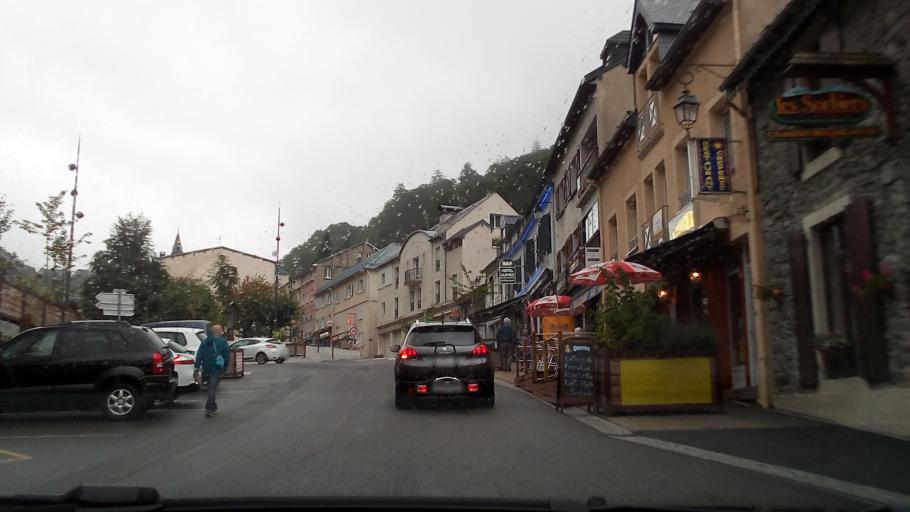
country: FR
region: Midi-Pyrenees
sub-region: Departement des Hautes-Pyrenees
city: Luz-Saint-Sauveur
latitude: 42.8961
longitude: 0.0626
